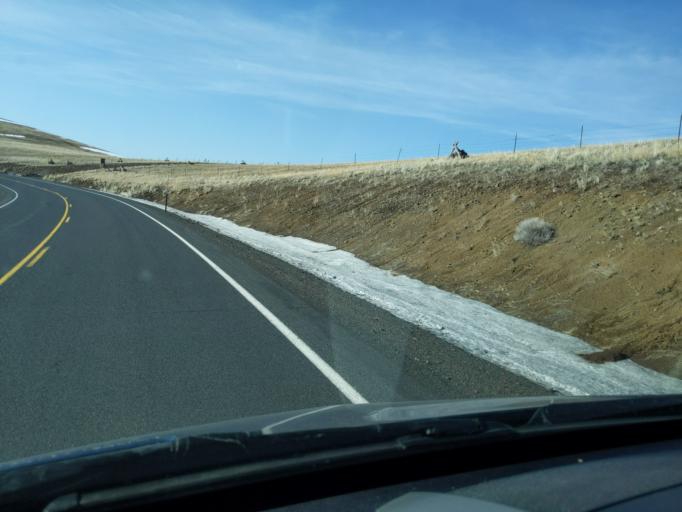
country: US
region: Oregon
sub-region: Umatilla County
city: Pilot Rock
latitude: 45.2993
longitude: -118.9867
